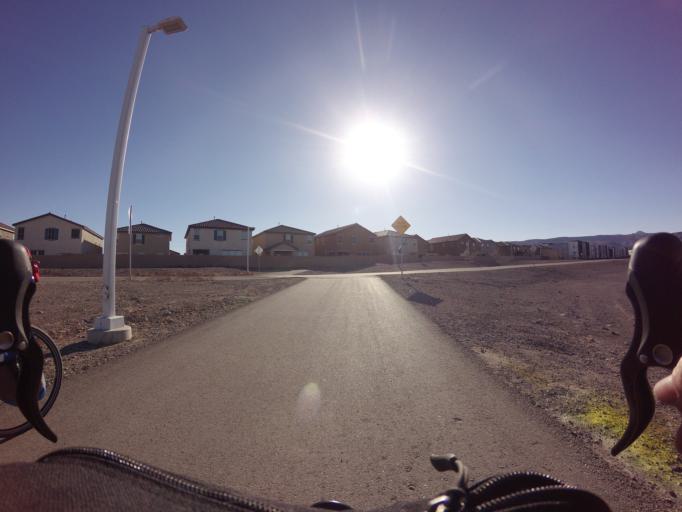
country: US
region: Nevada
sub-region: Clark County
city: Whitney
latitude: 36.0383
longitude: -115.0506
